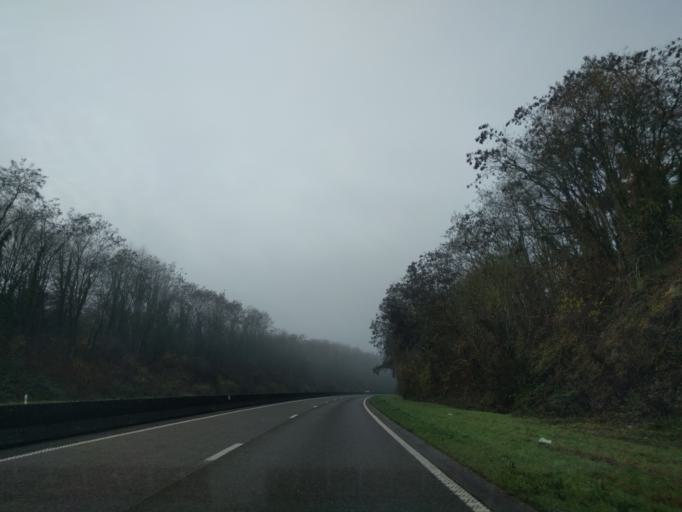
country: BE
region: Wallonia
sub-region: Province de Namur
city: Dinant
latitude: 50.2432
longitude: 4.9069
